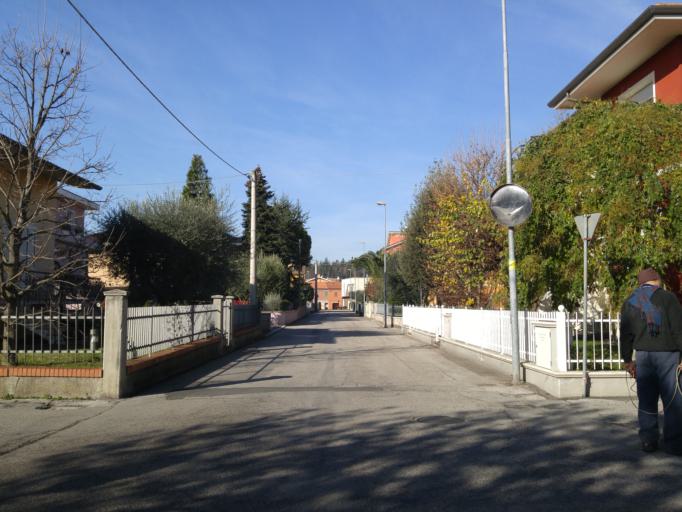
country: IT
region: The Marches
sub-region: Provincia di Pesaro e Urbino
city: Lucrezia
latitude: 43.7794
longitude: 12.9441
